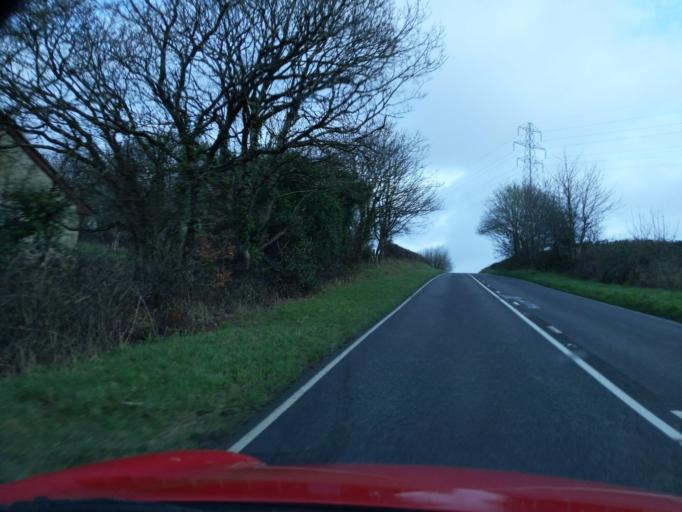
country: GB
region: England
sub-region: Devon
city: Holsworthy
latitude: 50.8920
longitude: -4.2736
